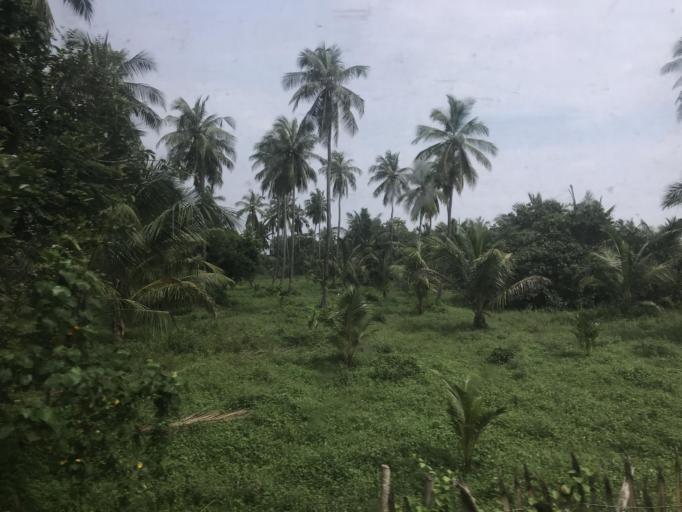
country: LK
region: Northern Province
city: Kilinochchi
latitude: 9.5922
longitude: 80.3453
